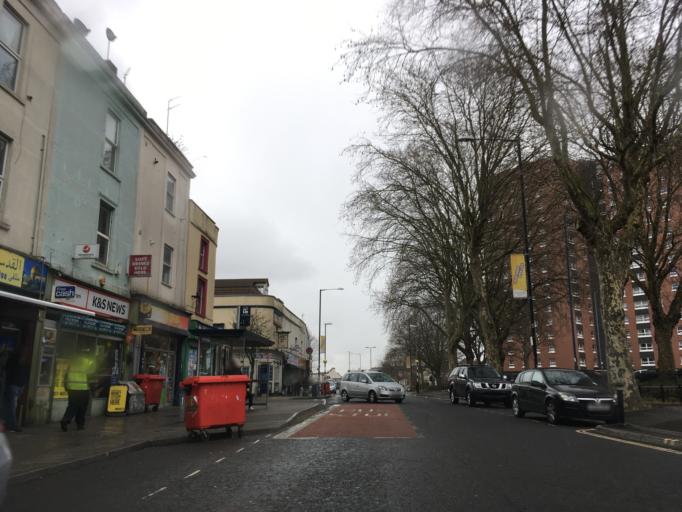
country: GB
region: England
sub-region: Bristol
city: Bristol
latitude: 51.4616
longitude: -2.5729
